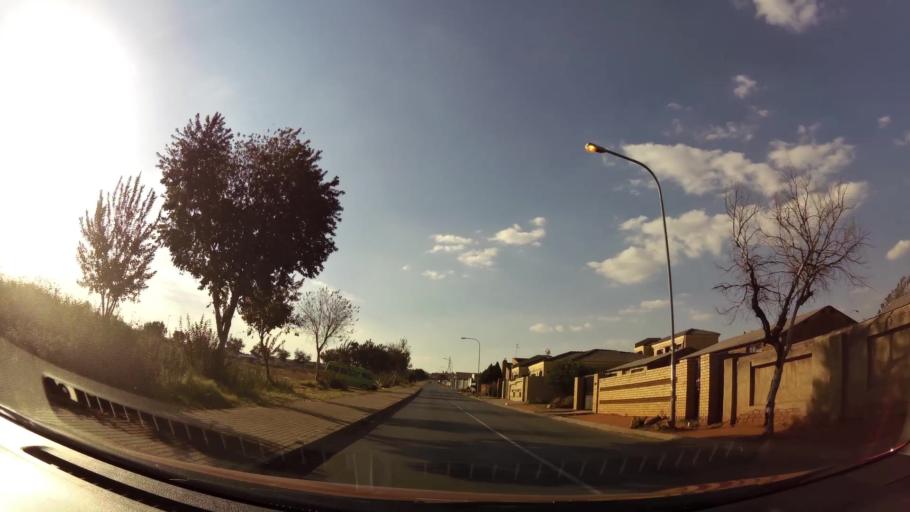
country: ZA
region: Gauteng
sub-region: City of Johannesburg Metropolitan Municipality
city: Roodepoort
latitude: -26.2071
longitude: 27.8779
